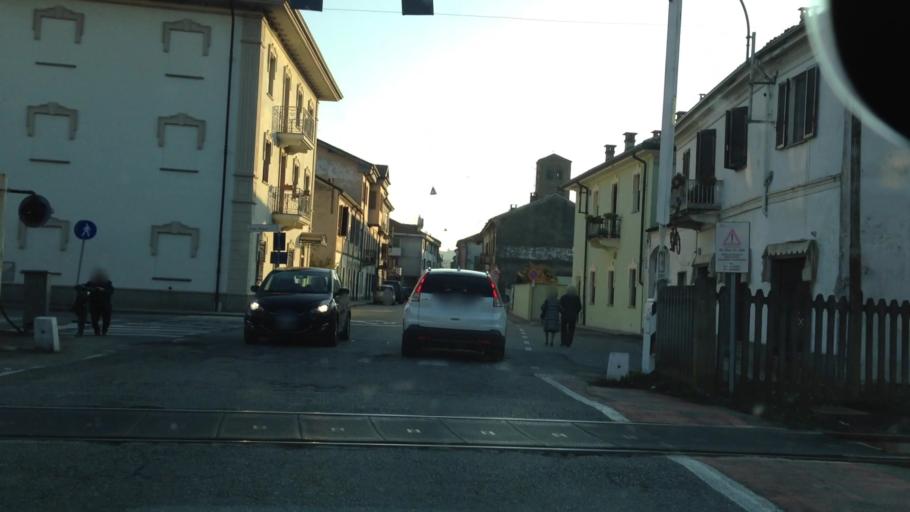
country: IT
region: Piedmont
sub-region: Provincia di Vercelli
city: Crescentino
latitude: 45.1944
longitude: 8.1034
